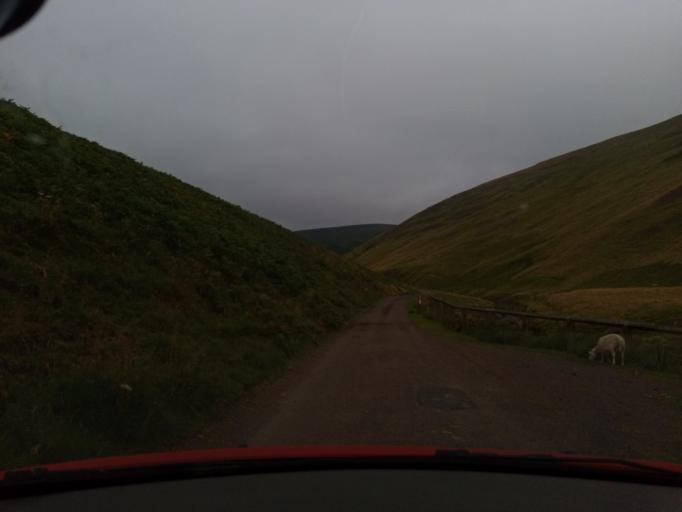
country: GB
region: England
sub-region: Northumberland
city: Rochester
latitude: 55.3965
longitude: -2.2227
